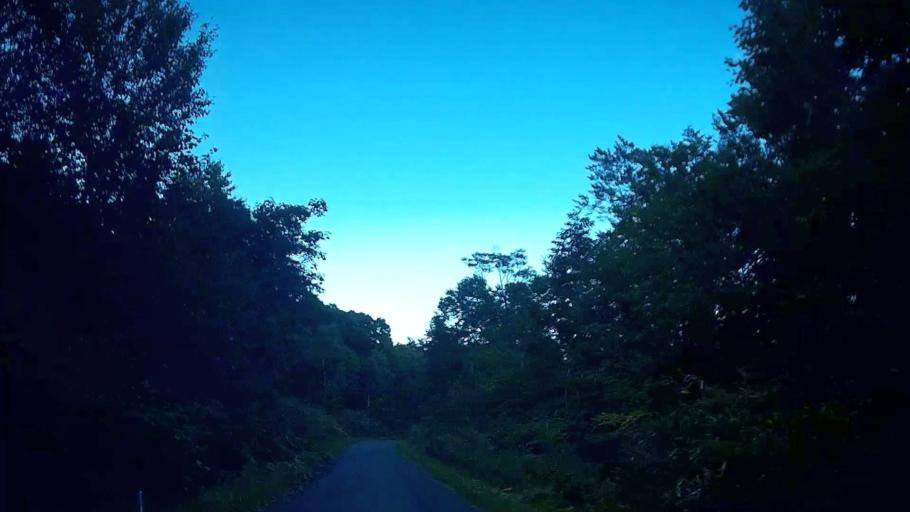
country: JP
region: Hokkaido
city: Iwanai
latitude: 42.5988
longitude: 139.9737
